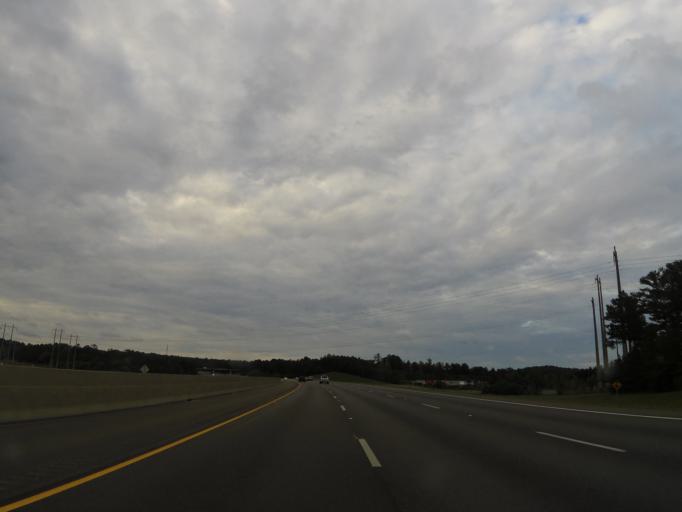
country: US
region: Alabama
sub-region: Jefferson County
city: Trussville
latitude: 33.5694
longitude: -86.6380
